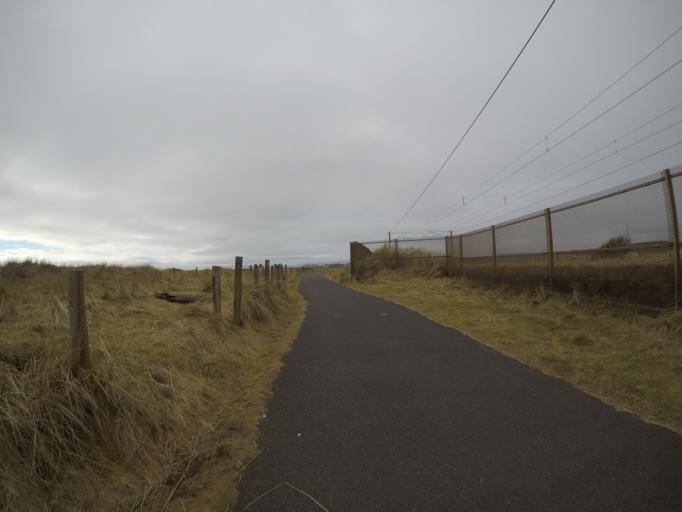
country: GB
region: Scotland
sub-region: North Ayrshire
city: Stevenston
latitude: 55.6325
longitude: -4.7657
